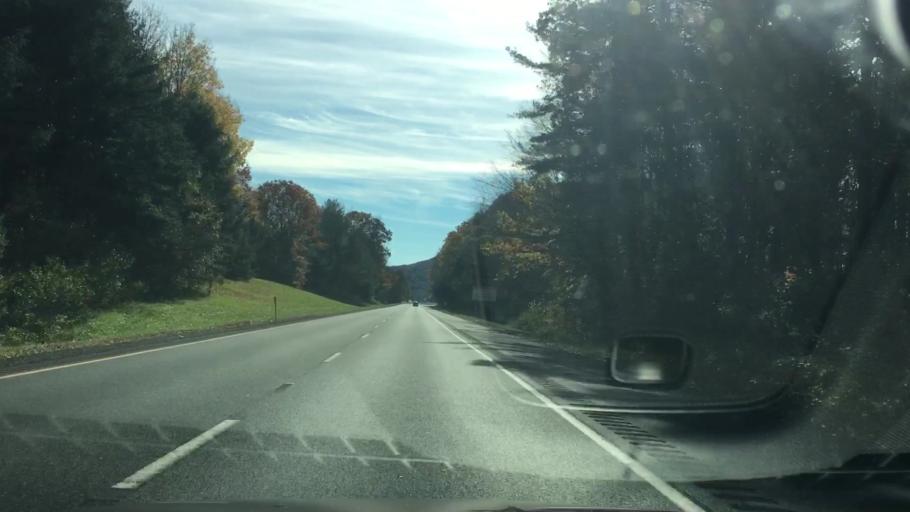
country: US
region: Massachusetts
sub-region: Franklin County
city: Bernardston
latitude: 42.7241
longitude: -72.5691
